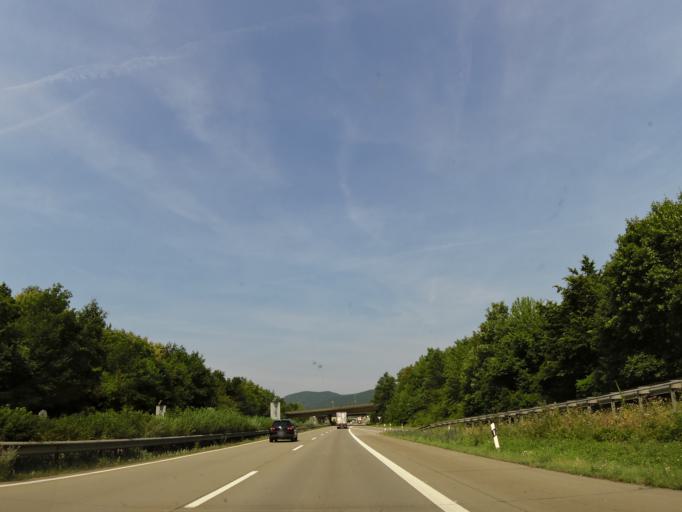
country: DE
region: Rheinland-Pfalz
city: Kruft
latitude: 50.3927
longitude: 7.3489
